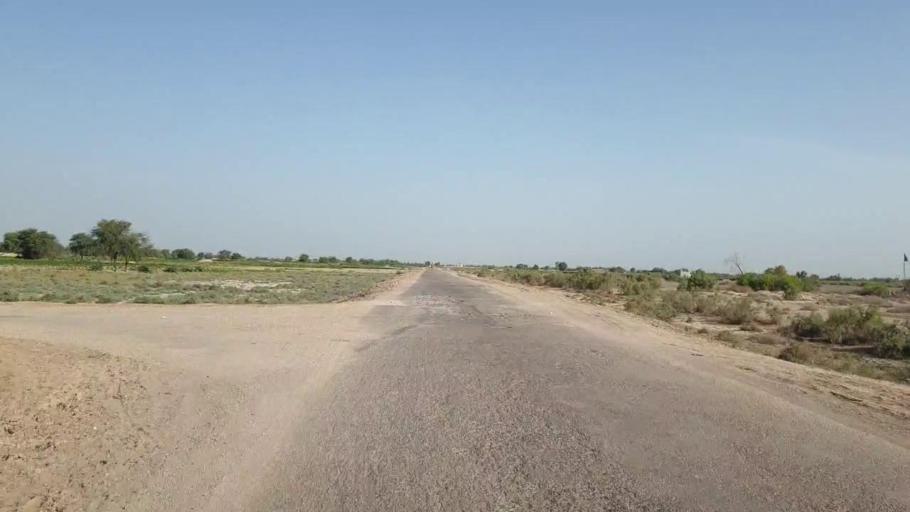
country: PK
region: Sindh
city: Nawabshah
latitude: 26.1504
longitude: 68.4480
